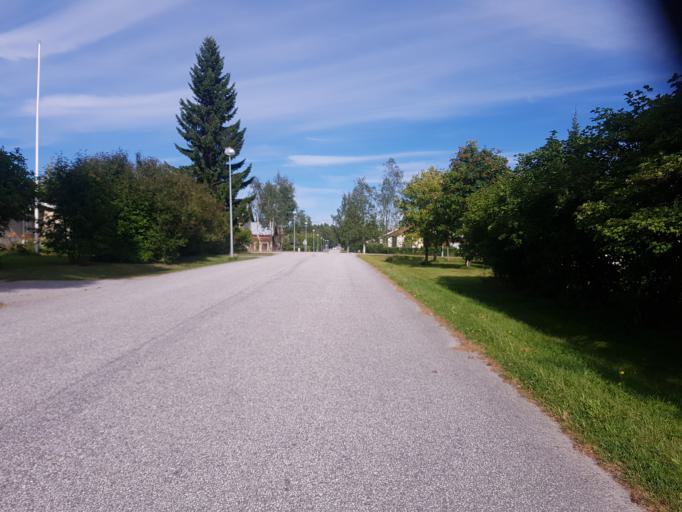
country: FI
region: Kainuu
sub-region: Kehys-Kainuu
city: Kuhmo
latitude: 64.1236
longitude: 29.5229
